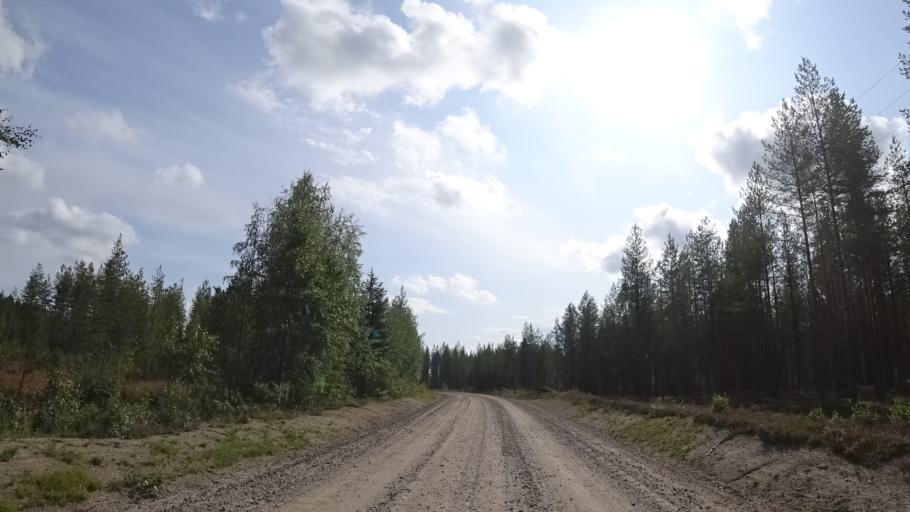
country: FI
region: North Karelia
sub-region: Pielisen Karjala
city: Lieksa
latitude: 63.5546
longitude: 30.0627
